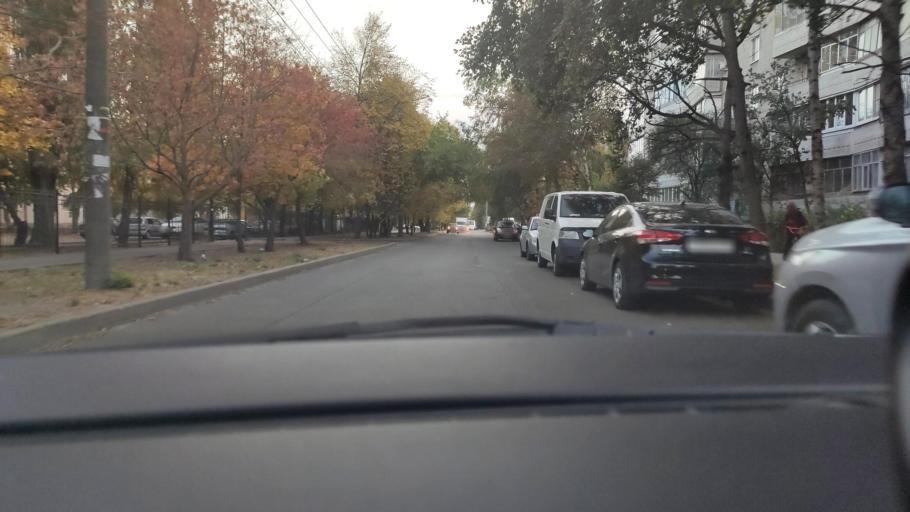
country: RU
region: Voronezj
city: Podgornoye
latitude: 51.7074
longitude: 39.1582
